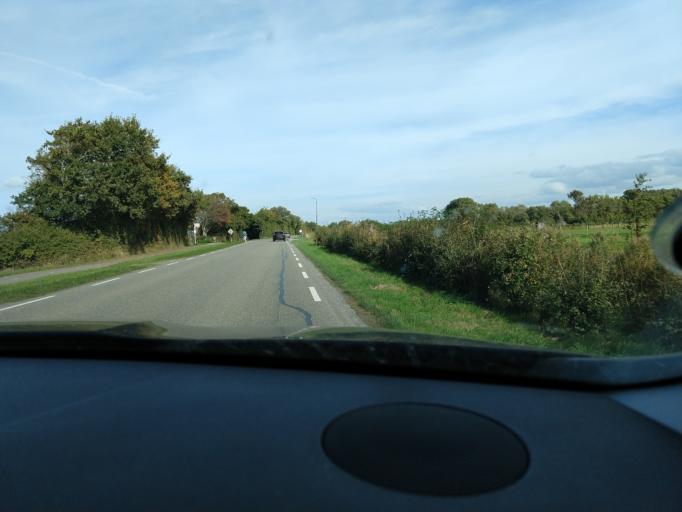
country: NL
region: Zeeland
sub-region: Gemeente Vlissingen
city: Vlissingen
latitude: 51.5353
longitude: 3.4775
